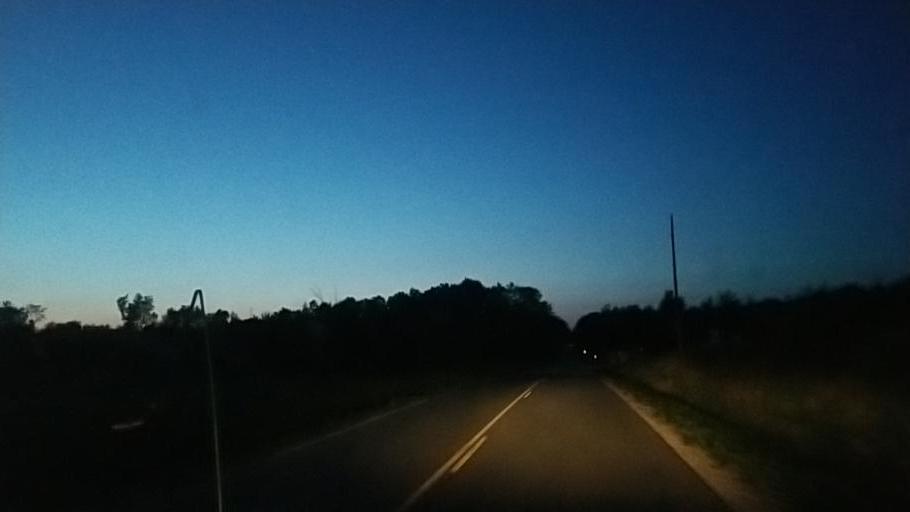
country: US
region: Michigan
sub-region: Osceola County
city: Reed City
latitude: 43.8788
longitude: -85.5623
